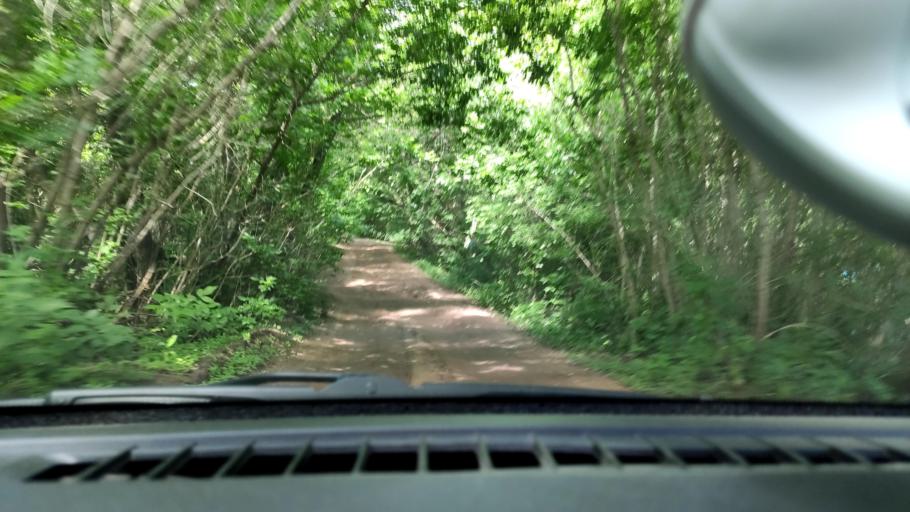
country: RU
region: Samara
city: Samara
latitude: 53.1277
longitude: 50.1807
